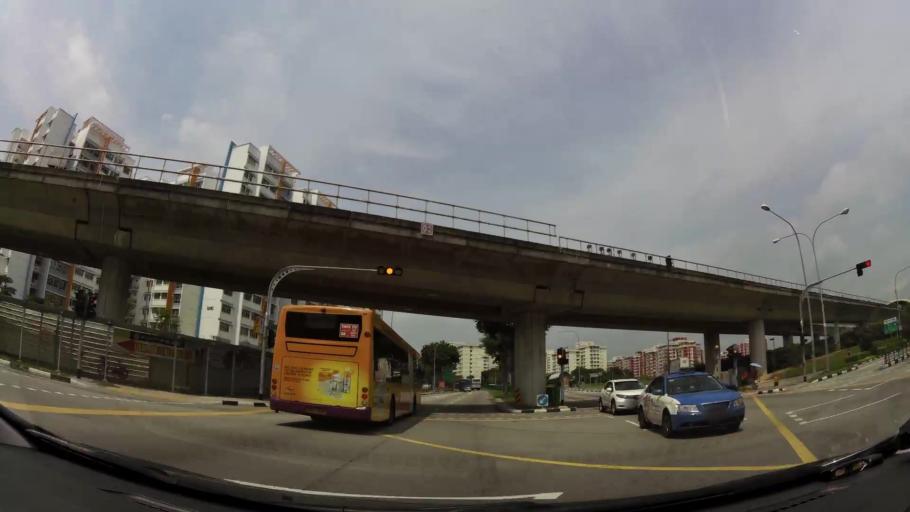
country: MY
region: Johor
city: Kampung Pasir Gudang Baru
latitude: 1.3708
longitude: 103.9489
